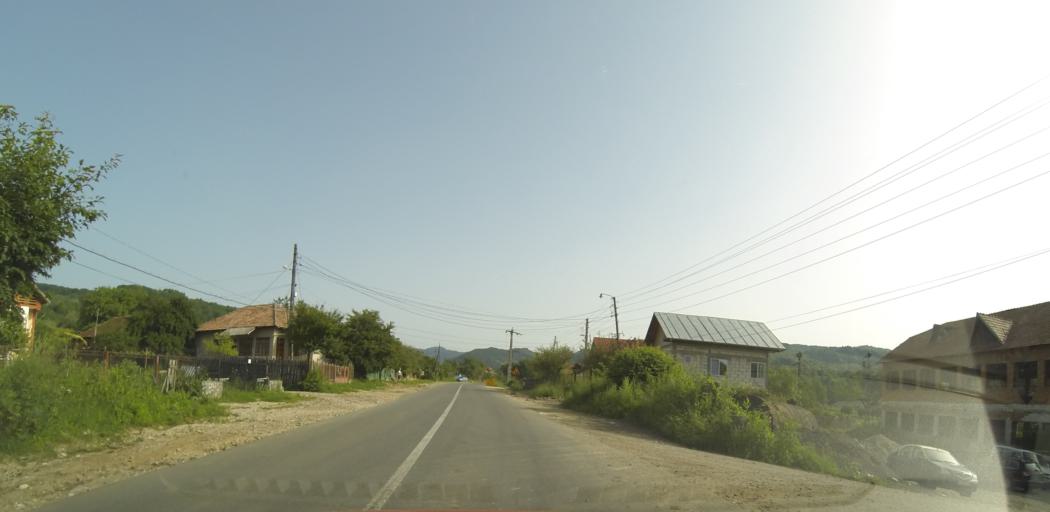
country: RO
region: Valcea
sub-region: Oras Baile Olanesti
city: Olanesti
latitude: 45.1691
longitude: 24.2578
